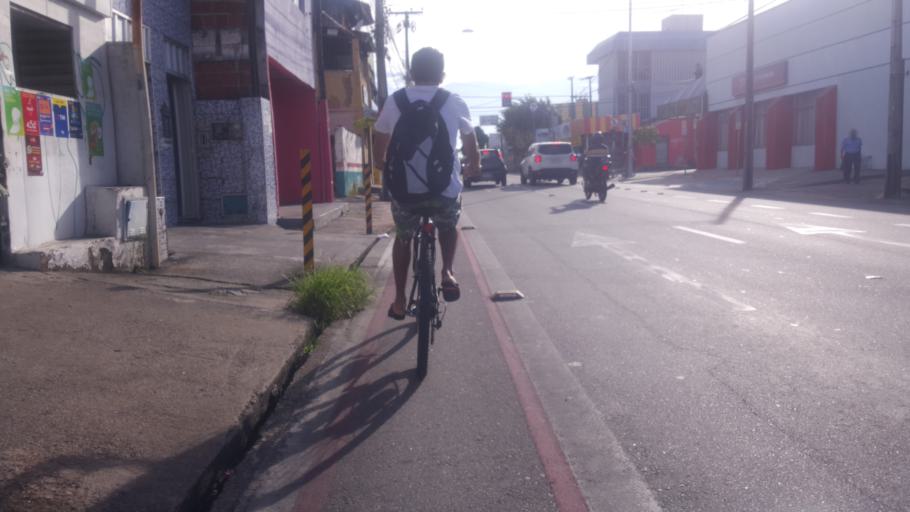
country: BR
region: Ceara
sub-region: Fortaleza
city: Fortaleza
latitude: -3.7584
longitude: -38.5433
